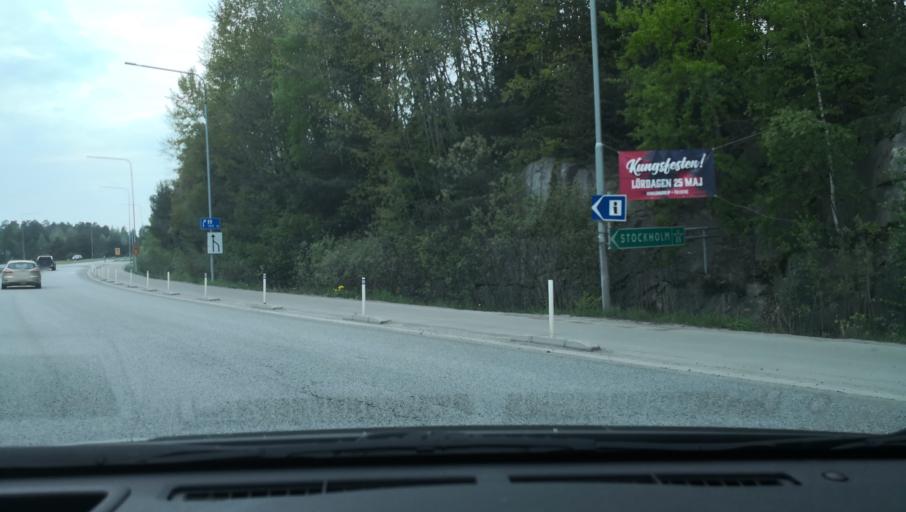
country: SE
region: Stockholm
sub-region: Upplands-Bro Kommun
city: Kungsaengen
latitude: 59.4943
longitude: 17.7428
